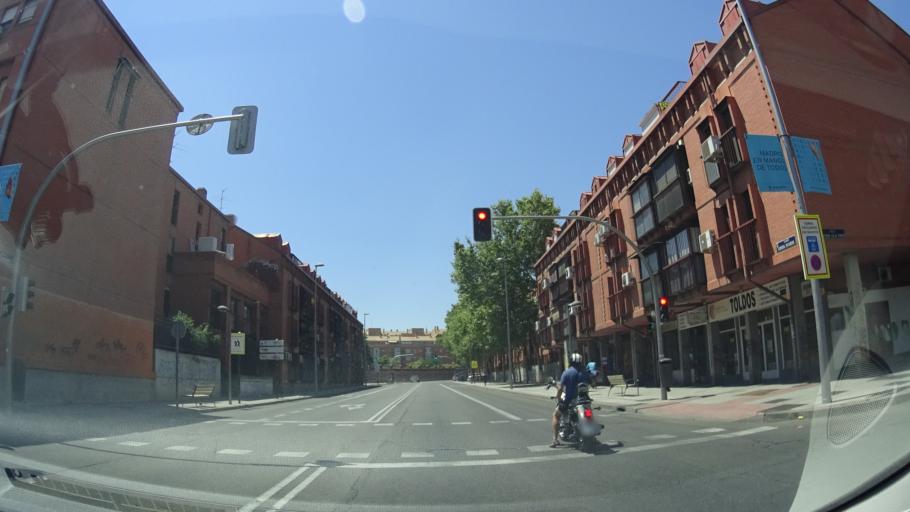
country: ES
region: Madrid
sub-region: Provincia de Madrid
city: Latina
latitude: 40.3817
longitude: -3.7443
